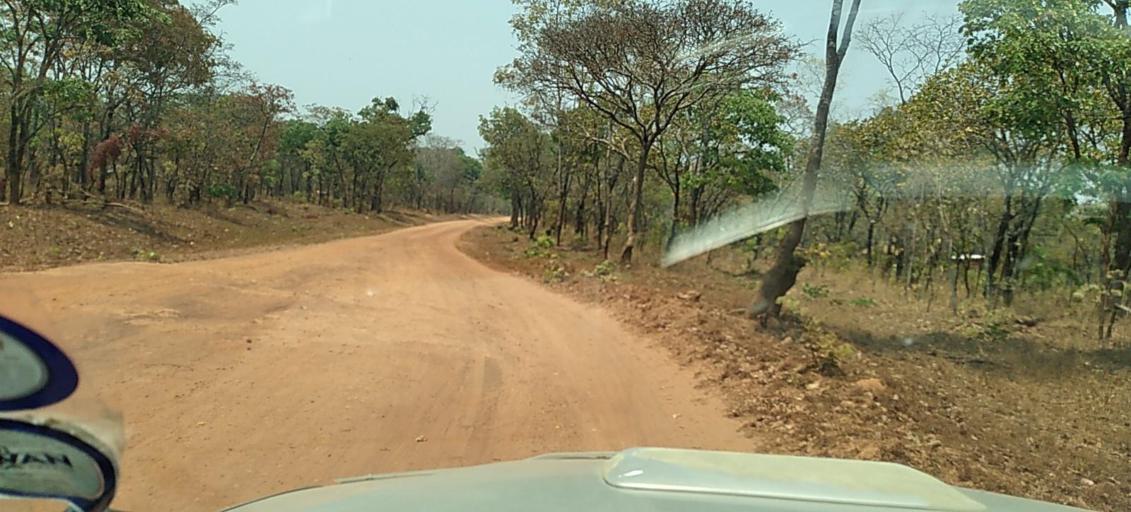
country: ZM
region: North-Western
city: Kasempa
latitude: -13.5638
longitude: 26.0900
